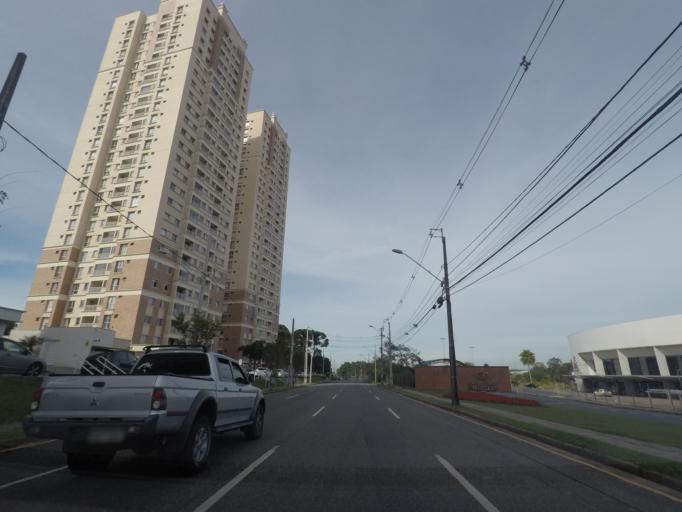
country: BR
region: Parana
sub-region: Curitiba
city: Curitiba
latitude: -25.4457
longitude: -49.3556
